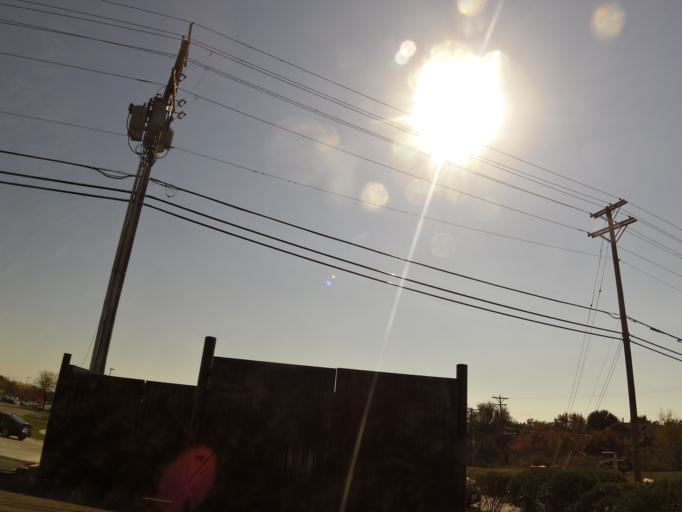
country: US
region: Kentucky
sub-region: Fayette County
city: Lexington
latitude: 37.9988
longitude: -84.4448
